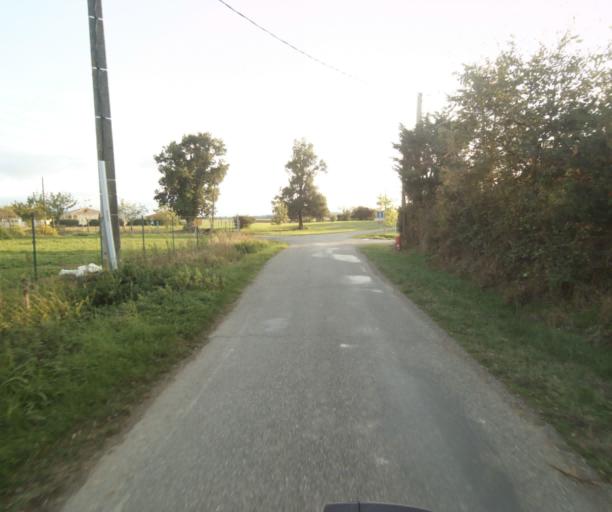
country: FR
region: Midi-Pyrenees
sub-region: Departement du Tarn-et-Garonne
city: Verdun-sur-Garonne
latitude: 43.8235
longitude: 1.1581
